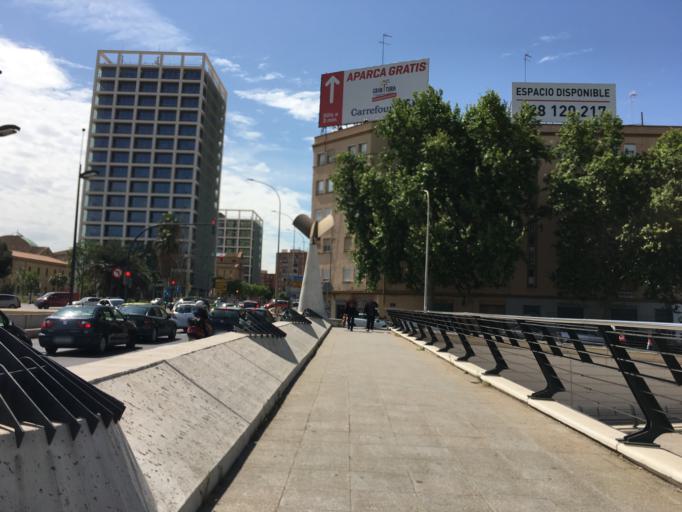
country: ES
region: Valencia
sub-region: Provincia de Valencia
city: Mislata
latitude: 39.4735
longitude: -0.4060
